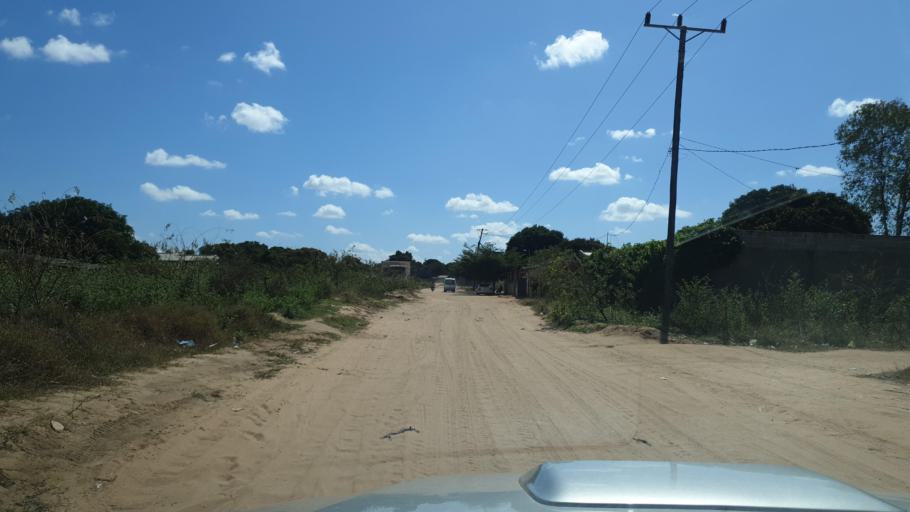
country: MZ
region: Nampula
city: Nampula
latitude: -15.1034
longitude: 39.2061
